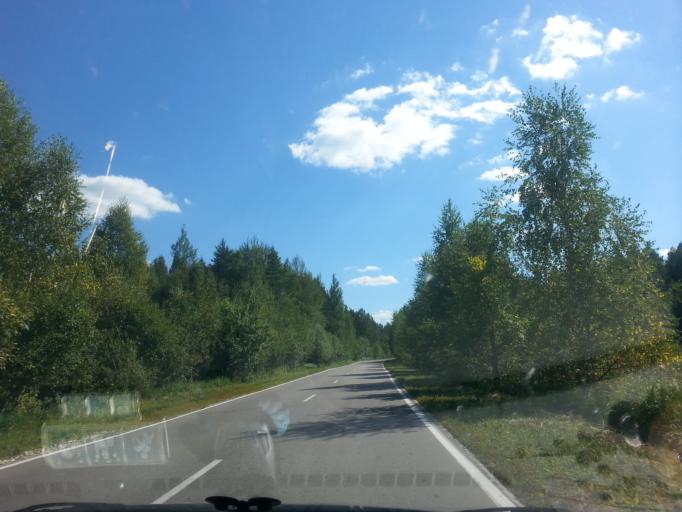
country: RU
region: Vladimir
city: Galitsy
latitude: 56.1344
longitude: 42.8738
